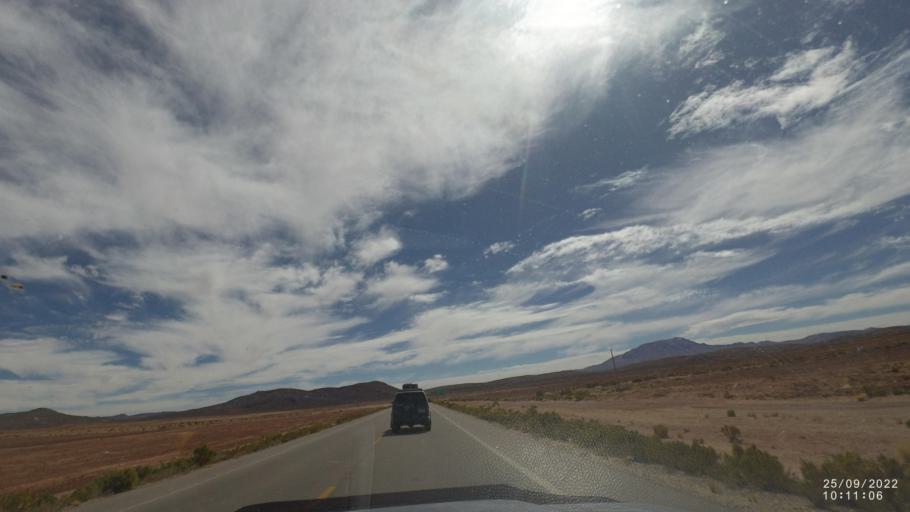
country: BO
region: Potosi
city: Colchani
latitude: -20.1048
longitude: -66.9069
